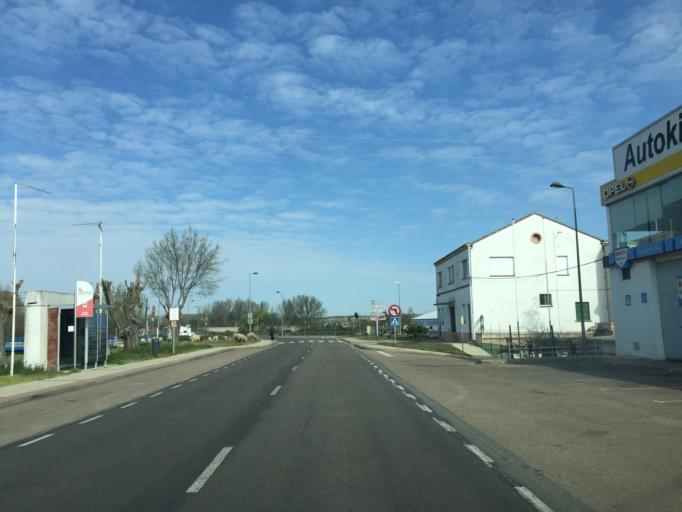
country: ES
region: Castille and Leon
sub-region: Provincia de Salamanca
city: Ciudad Rodrigo
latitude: 40.5916
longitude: -6.5382
